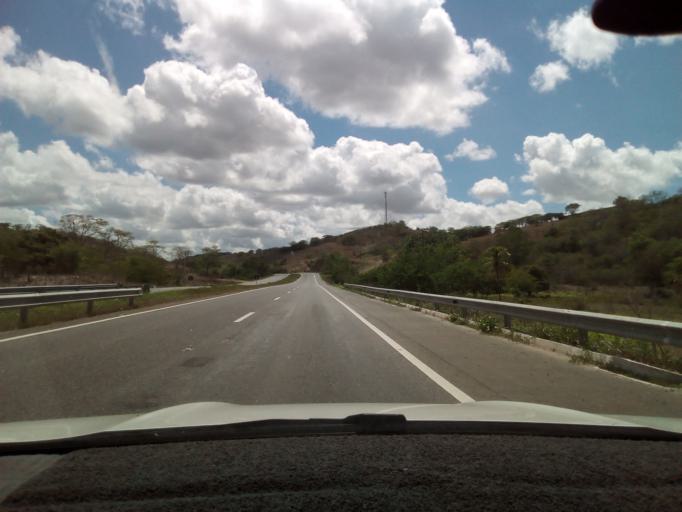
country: BR
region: Paraiba
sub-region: Fagundes
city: Fagundes
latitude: -7.2801
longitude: -35.7614
